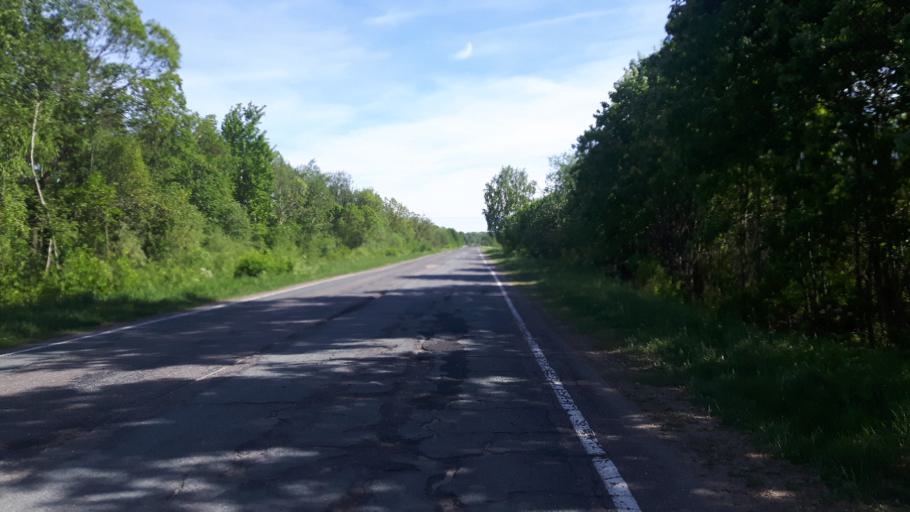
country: RU
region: Leningrad
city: Ivangorod
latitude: 59.4203
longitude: 28.3212
